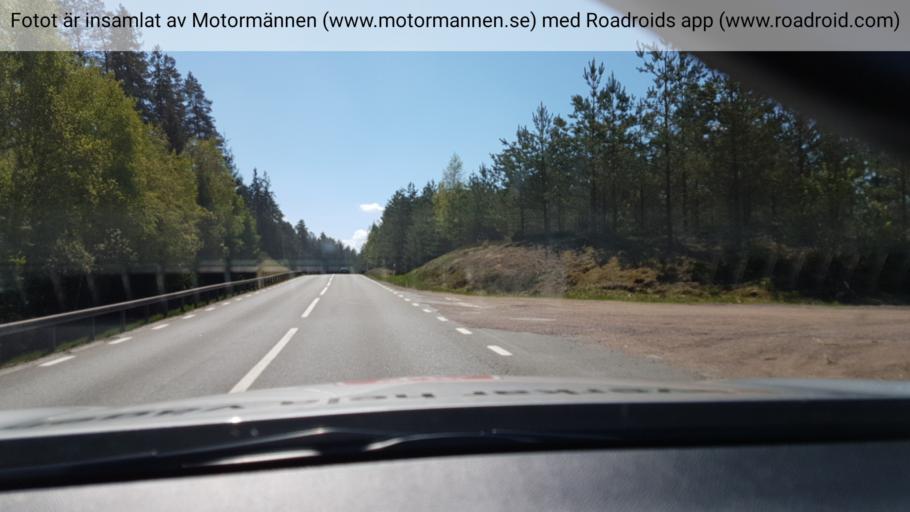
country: SE
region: Joenkoeping
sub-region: Mullsjo Kommun
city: Mullsjoe
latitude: 57.7885
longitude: 13.8359
